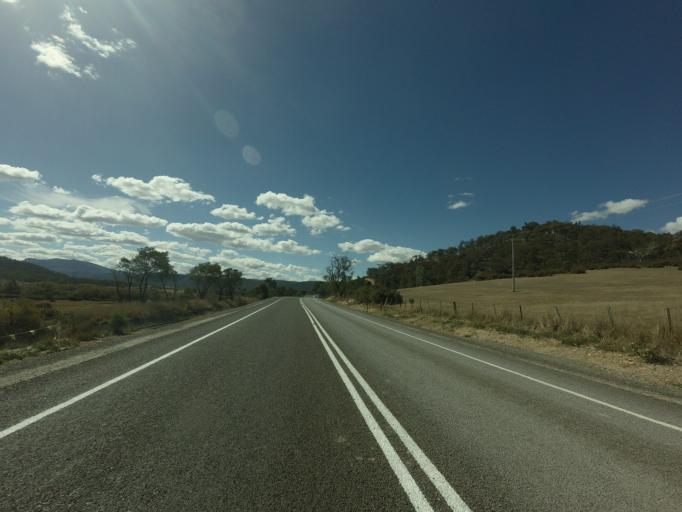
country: AU
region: Tasmania
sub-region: Break O'Day
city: St Helens
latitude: -41.6618
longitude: 147.9141
